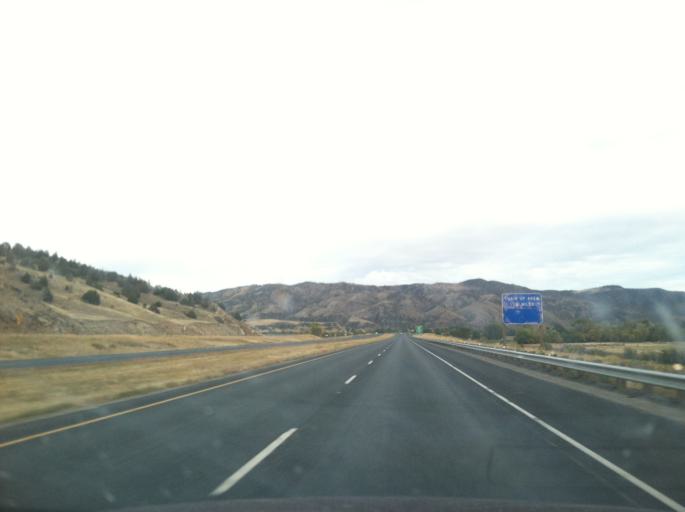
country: US
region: Montana
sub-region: Jefferson County
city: Whitehall
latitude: 45.8712
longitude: -111.9655
